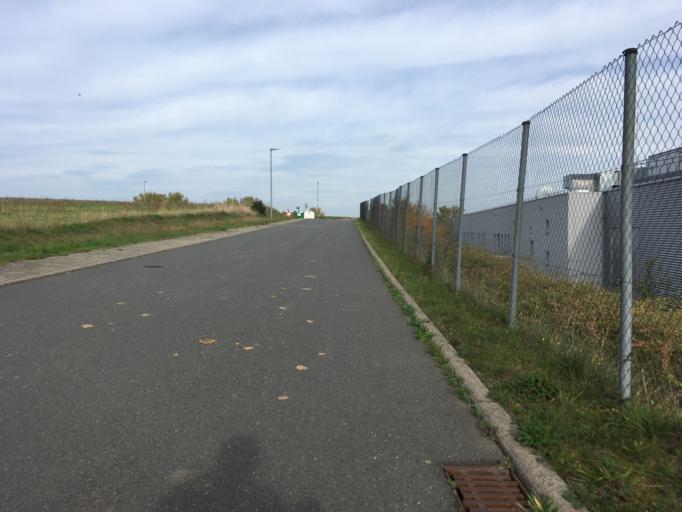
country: DE
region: Baden-Wuerttemberg
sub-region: Karlsruhe Region
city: Rosenberg
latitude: 49.4627
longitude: 9.4758
